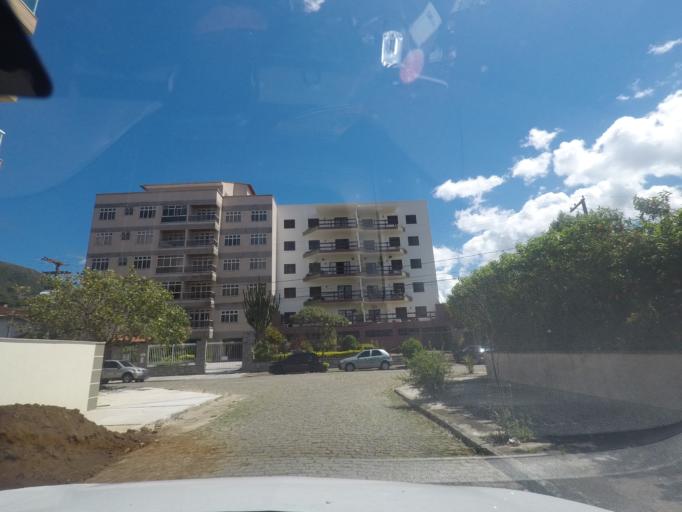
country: BR
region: Rio de Janeiro
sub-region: Teresopolis
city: Teresopolis
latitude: -22.4330
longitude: -42.9764
